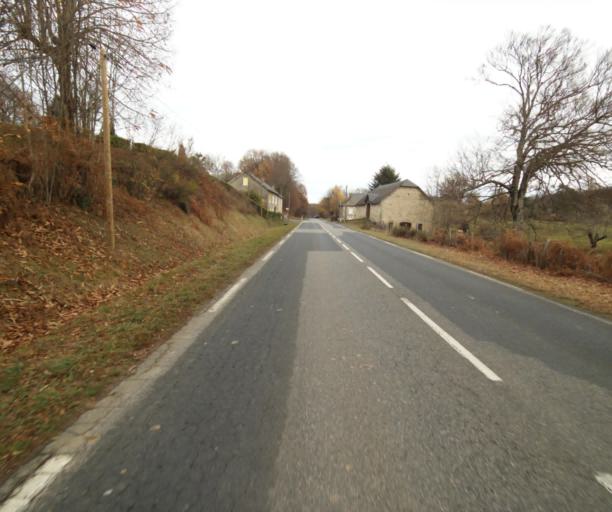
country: FR
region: Limousin
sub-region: Departement de la Correze
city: Sainte-Fortunade
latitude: 45.1890
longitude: 1.7677
